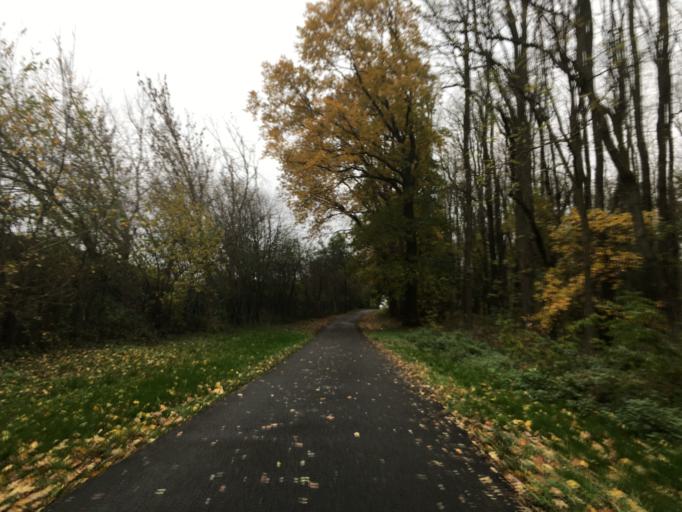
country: DE
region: Brandenburg
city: Frankfurt (Oder)
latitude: 52.3011
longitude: 14.5248
